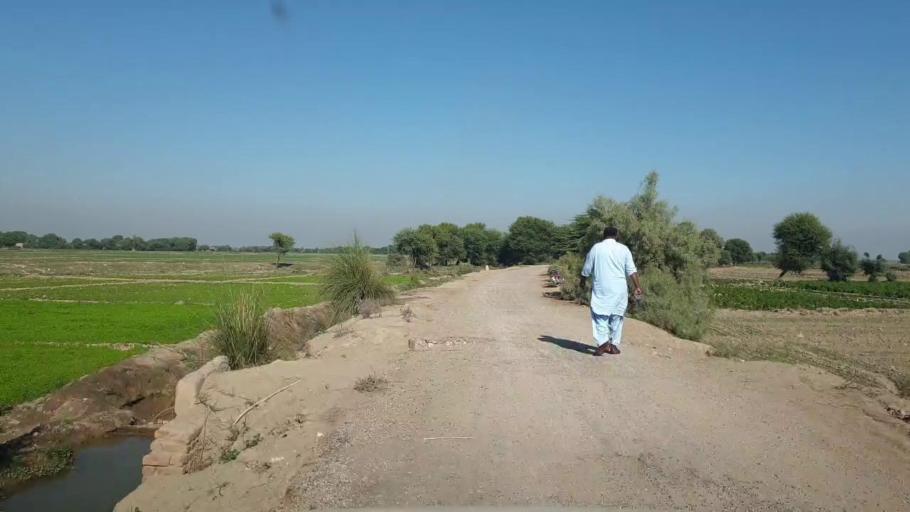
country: PK
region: Sindh
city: Dadu
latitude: 26.7919
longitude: 67.8240
